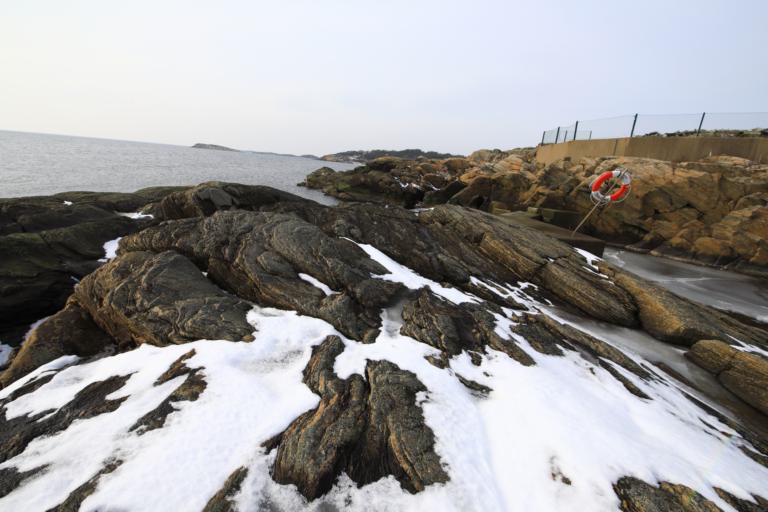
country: SE
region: Halland
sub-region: Kungsbacka Kommun
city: Frillesas
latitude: 57.2138
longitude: 12.1612
